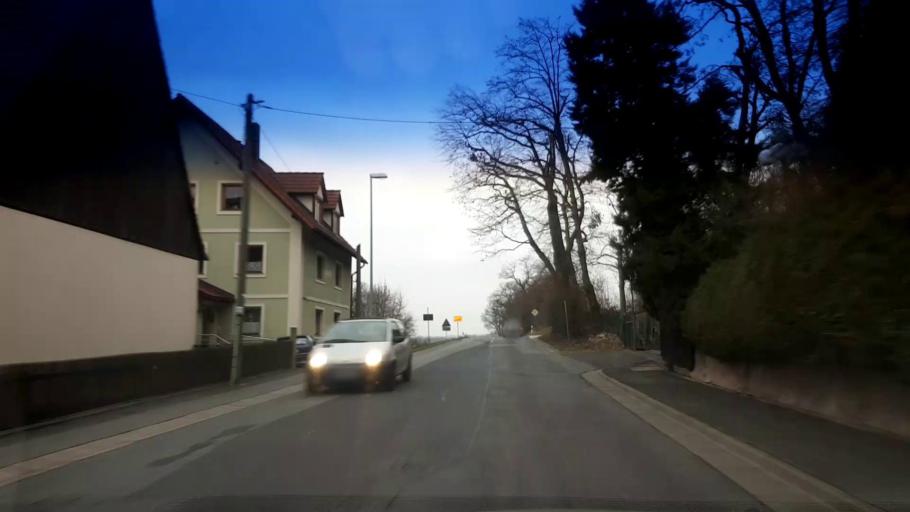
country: DE
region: Bavaria
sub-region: Upper Franconia
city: Pettstadt
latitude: 49.7987
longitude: 10.9206
